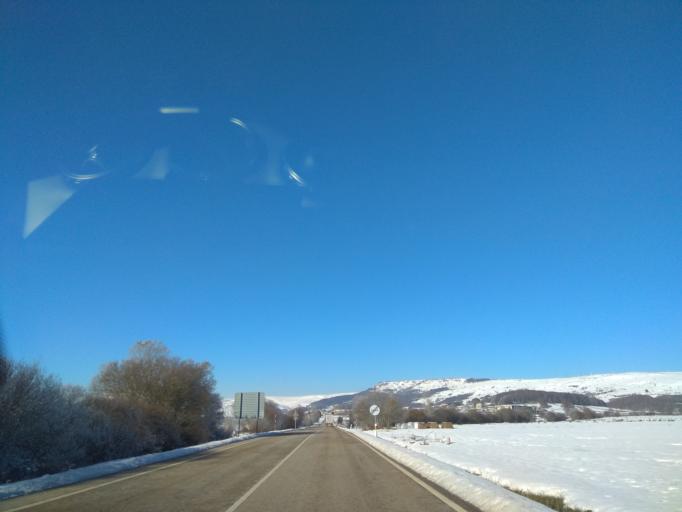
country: ES
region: Castille and Leon
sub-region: Provincia de Burgos
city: Arija
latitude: 43.0100
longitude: -3.8461
